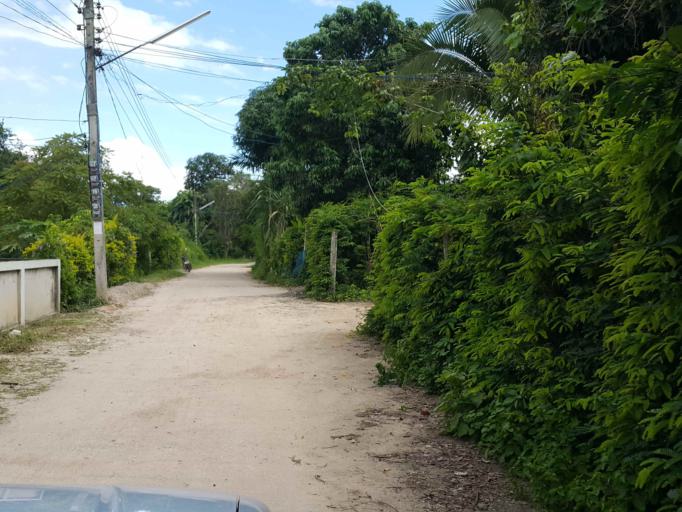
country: TH
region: Chiang Mai
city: San Sai
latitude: 18.9422
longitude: 98.9196
